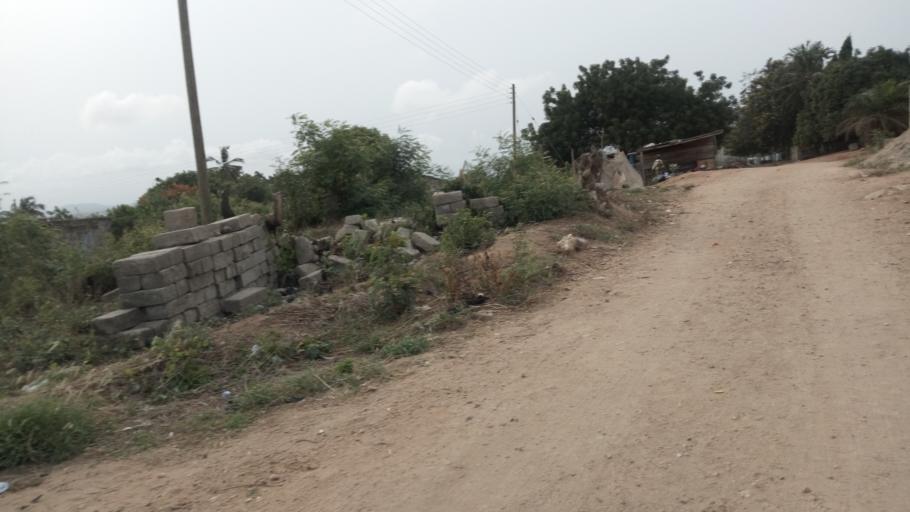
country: GH
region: Central
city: Winneba
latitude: 5.3577
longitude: -0.6278
